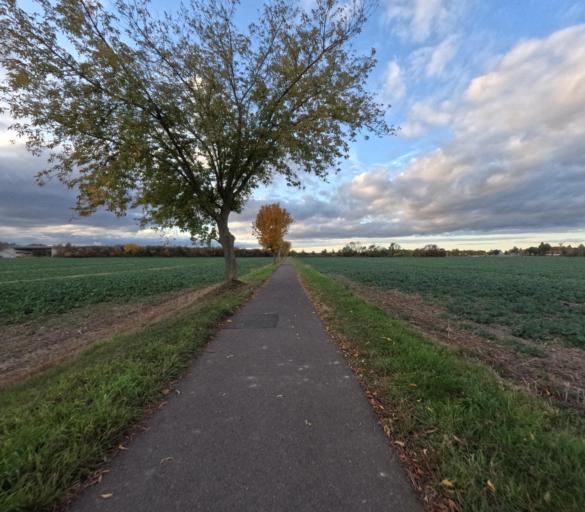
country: DE
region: Saxony
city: Naunhof
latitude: 51.2579
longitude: 12.6263
